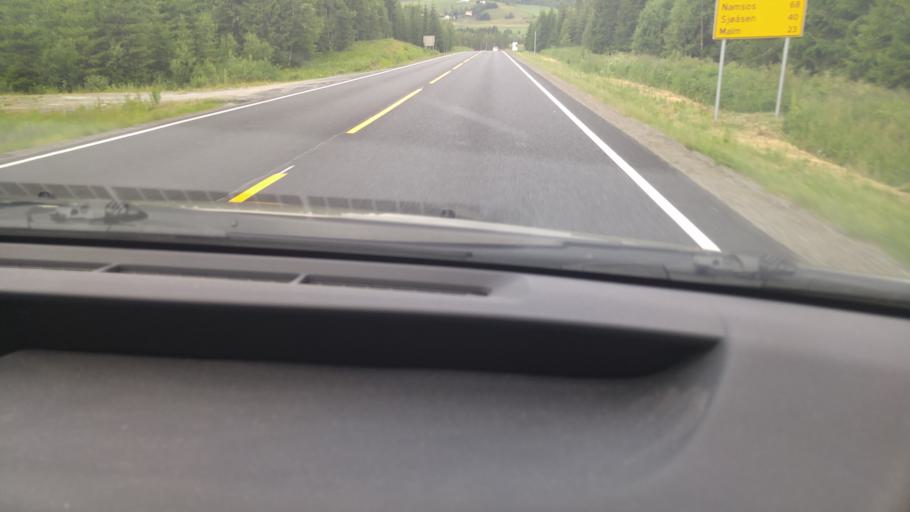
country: NO
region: Nord-Trondelag
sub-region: Steinkjer
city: Steinkjer
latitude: 64.0696
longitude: 11.5063
